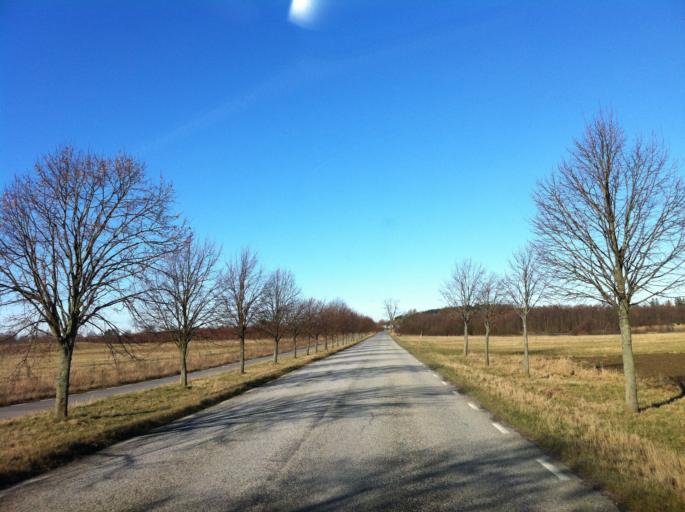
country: SE
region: Skane
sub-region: Svedala Kommun
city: Klagerup
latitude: 55.5694
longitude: 13.2028
